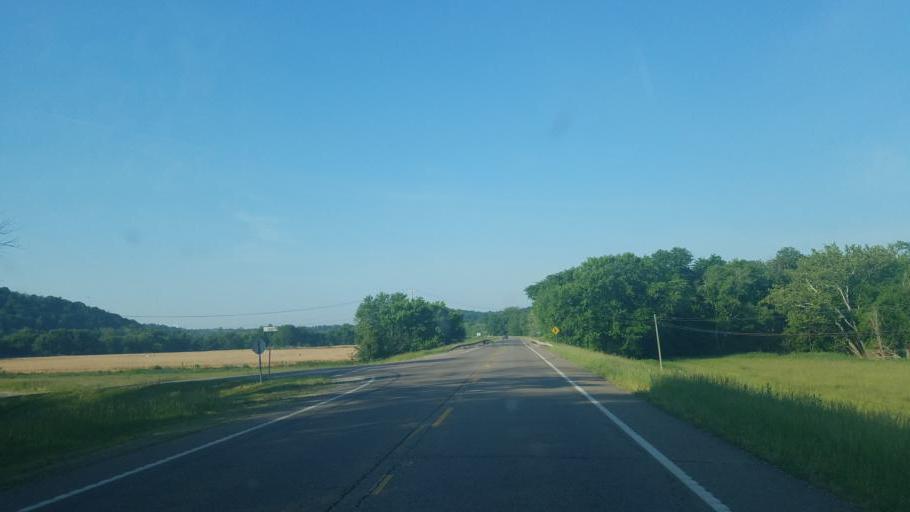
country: US
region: West Virginia
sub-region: Mason County
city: New Haven
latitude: 39.1053
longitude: -81.9225
